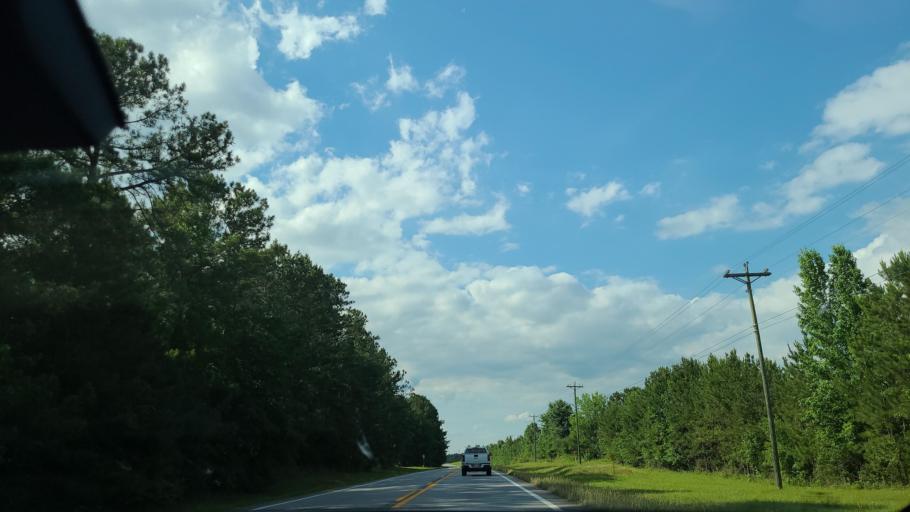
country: US
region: Georgia
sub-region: Jones County
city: Gray
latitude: 33.0885
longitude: -83.4843
